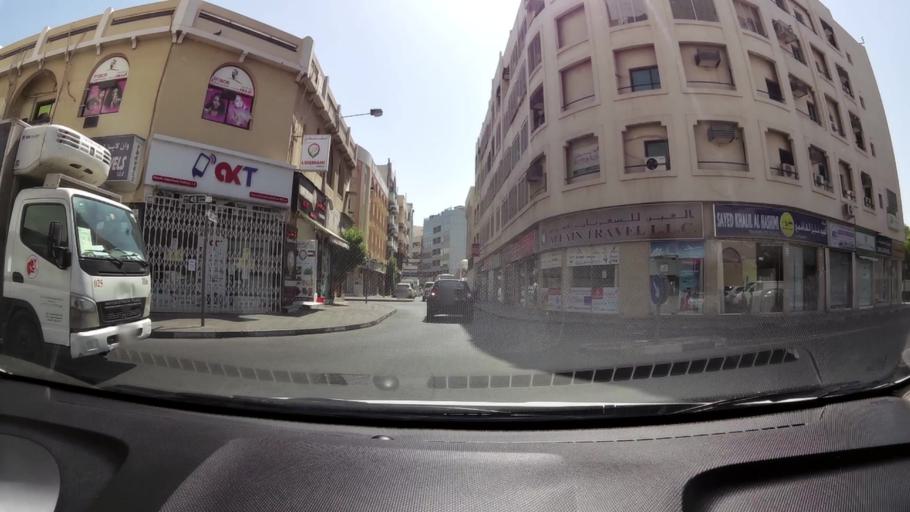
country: AE
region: Ash Shariqah
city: Sharjah
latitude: 25.2768
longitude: 55.3131
